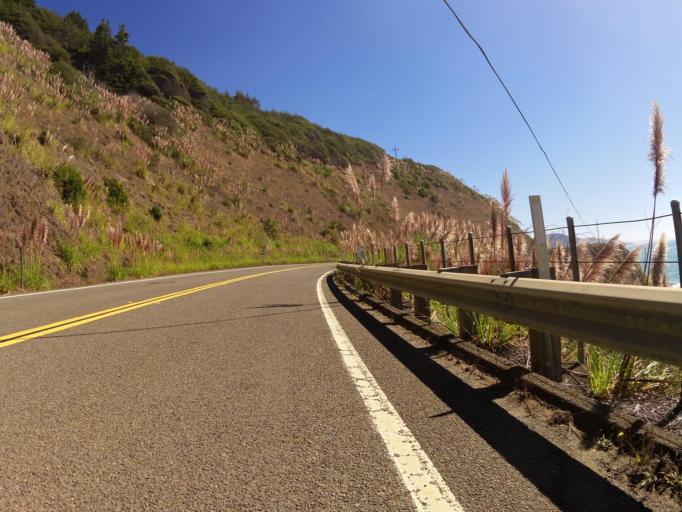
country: US
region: California
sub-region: Mendocino County
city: Fort Bragg
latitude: 39.6964
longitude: -123.7990
